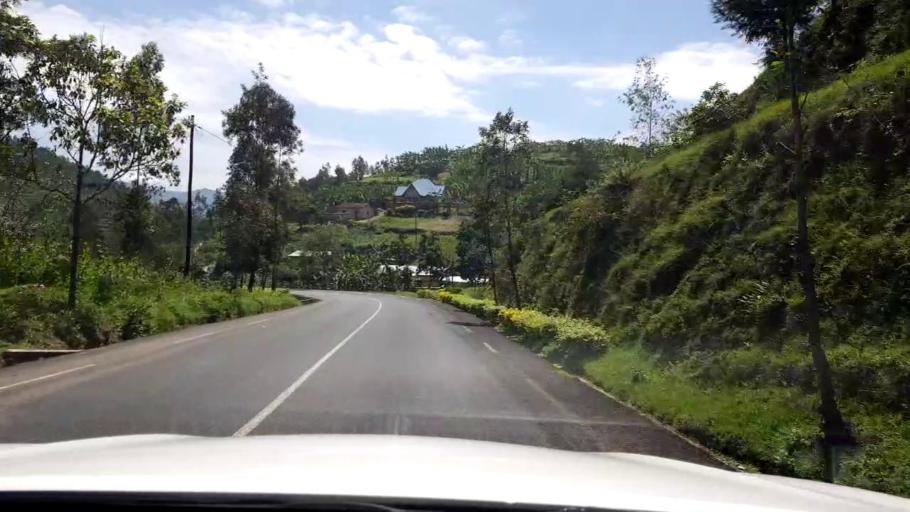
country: RW
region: Southern Province
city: Gitarama
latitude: -1.9197
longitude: 29.6431
